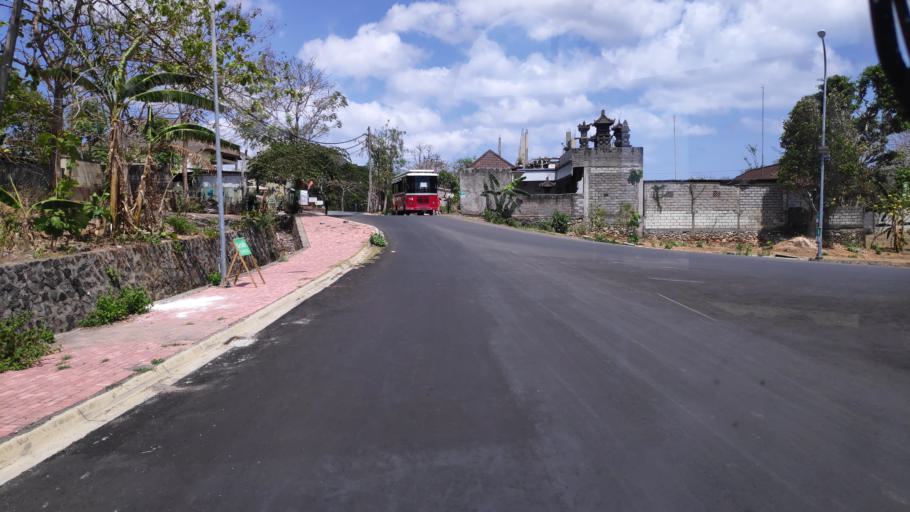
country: ID
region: Bali
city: Jimbaran
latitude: -8.8069
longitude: 115.1656
